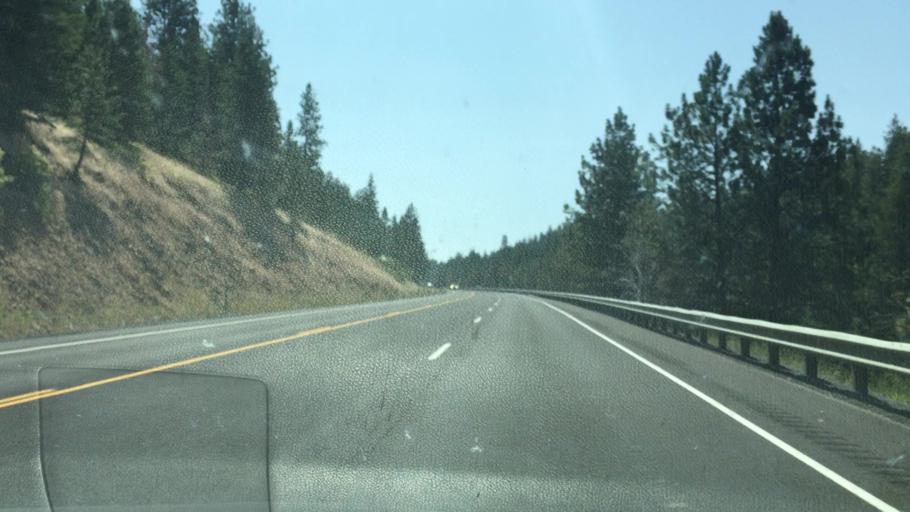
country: US
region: Idaho
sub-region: Idaho County
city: Grangeville
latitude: 45.8650
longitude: -116.2367
